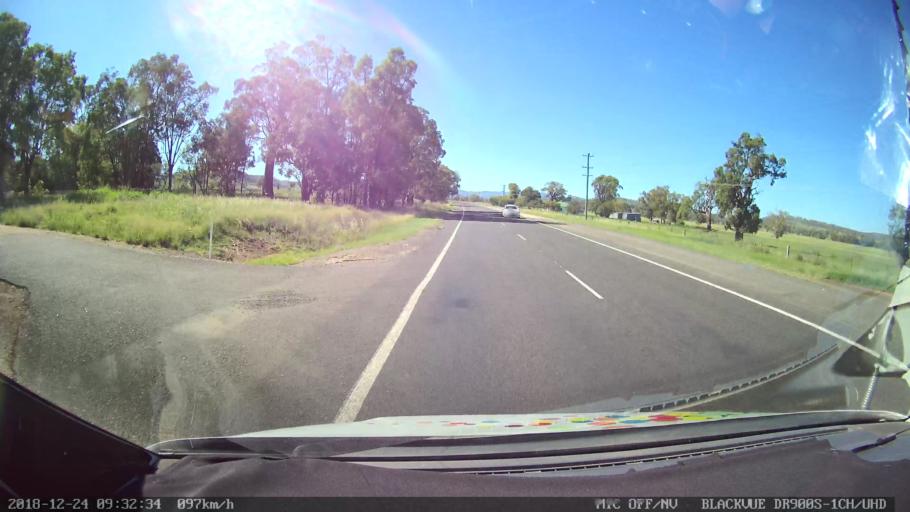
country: AU
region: New South Wales
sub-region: Liverpool Plains
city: Quirindi
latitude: -31.5921
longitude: 150.7032
